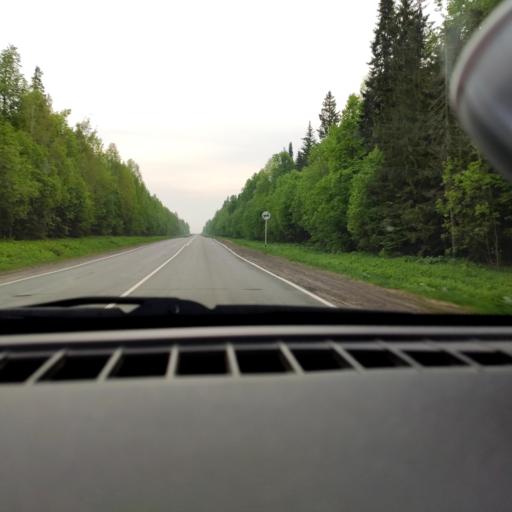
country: RU
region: Perm
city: Perm
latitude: 58.1874
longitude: 56.2184
